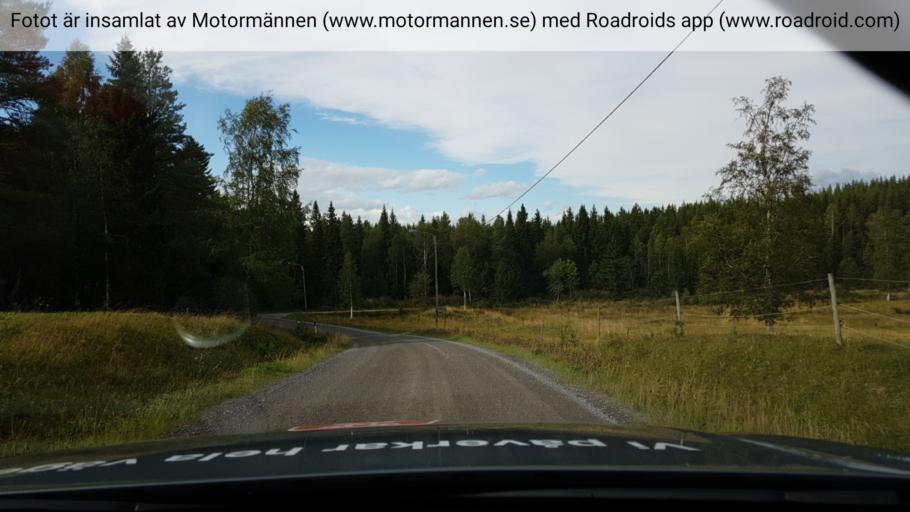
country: SE
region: Jaemtland
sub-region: Braecke Kommun
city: Braecke
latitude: 63.2834
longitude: 15.3707
